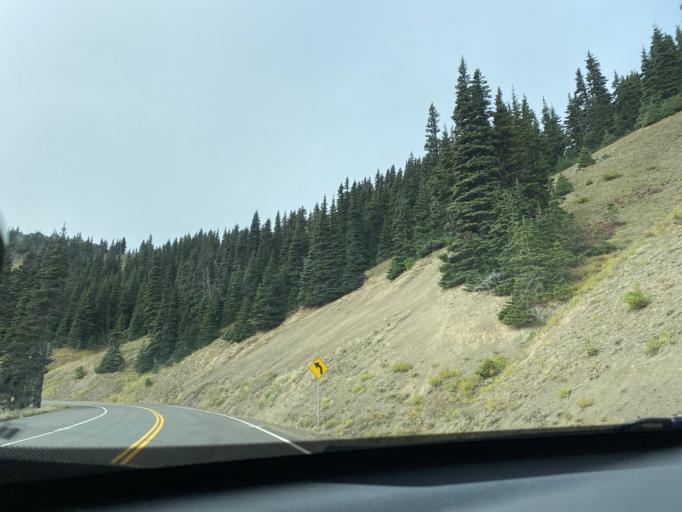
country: US
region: Washington
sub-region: Clallam County
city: Port Angeles
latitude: 47.9739
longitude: -123.4868
